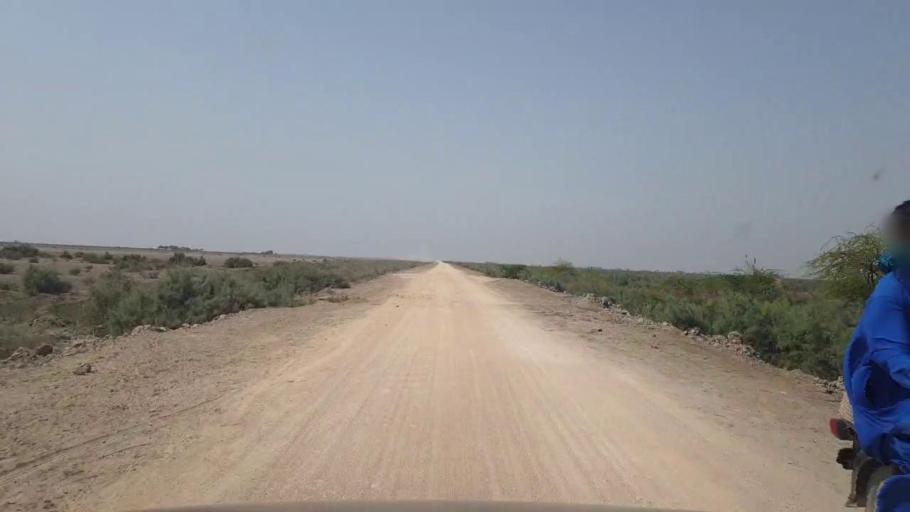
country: PK
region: Sindh
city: Jati
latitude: 24.3844
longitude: 68.5929
